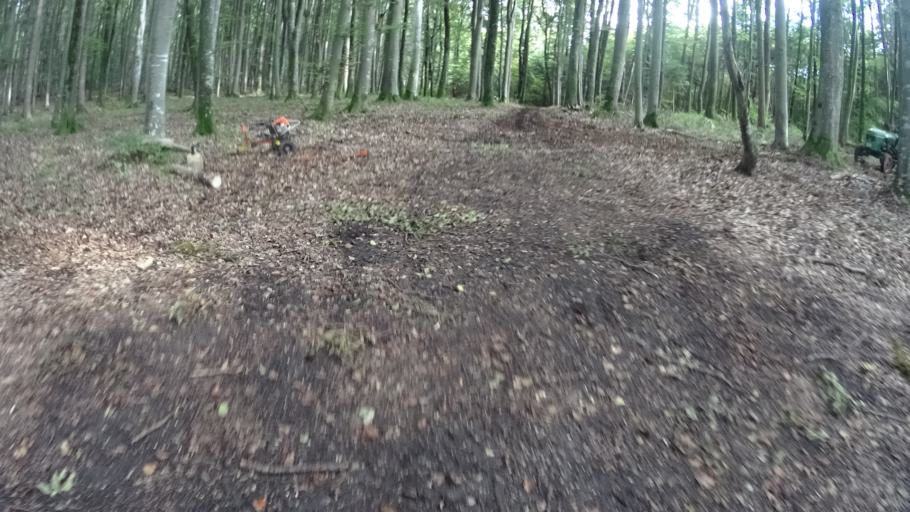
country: DE
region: Bavaria
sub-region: Upper Bavaria
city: Walting
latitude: 48.9066
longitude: 11.3067
